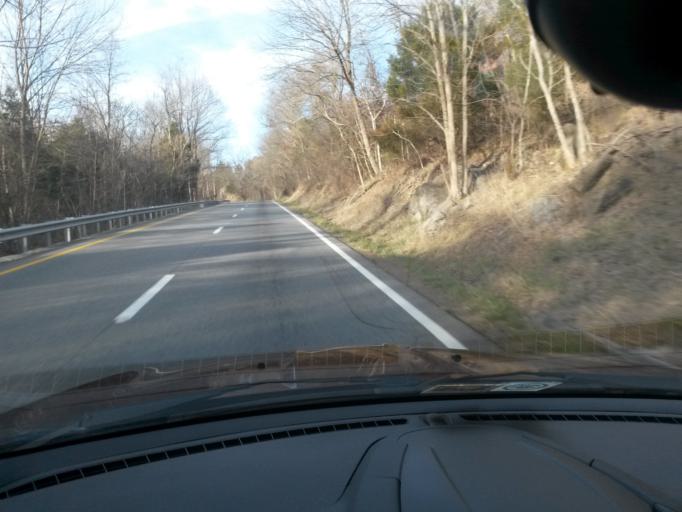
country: US
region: Virginia
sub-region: Botetourt County
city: Fincastle
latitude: 37.5920
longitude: -79.8349
